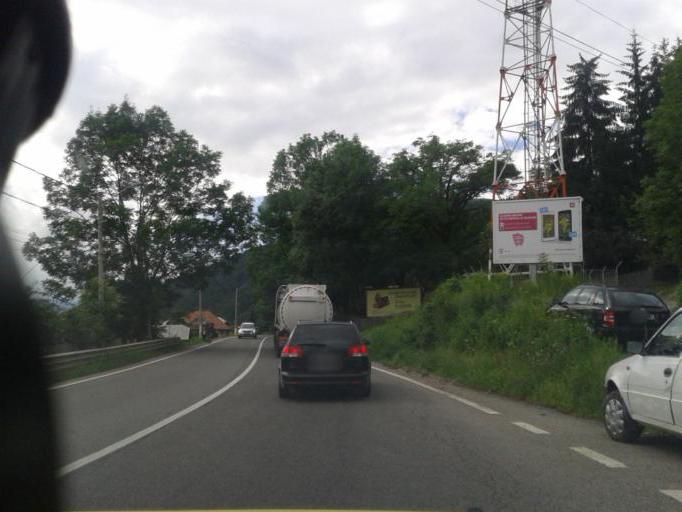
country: RO
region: Prahova
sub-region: Comuna Comarnic
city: Posada
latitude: 45.2853
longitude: 25.6192
